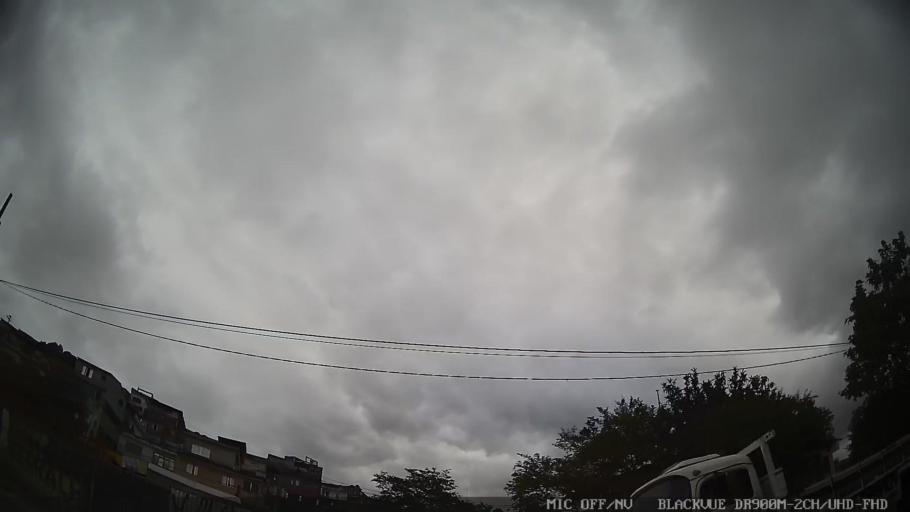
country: BR
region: Sao Paulo
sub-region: Sao Paulo
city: Sao Paulo
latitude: -23.4786
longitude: -46.7075
